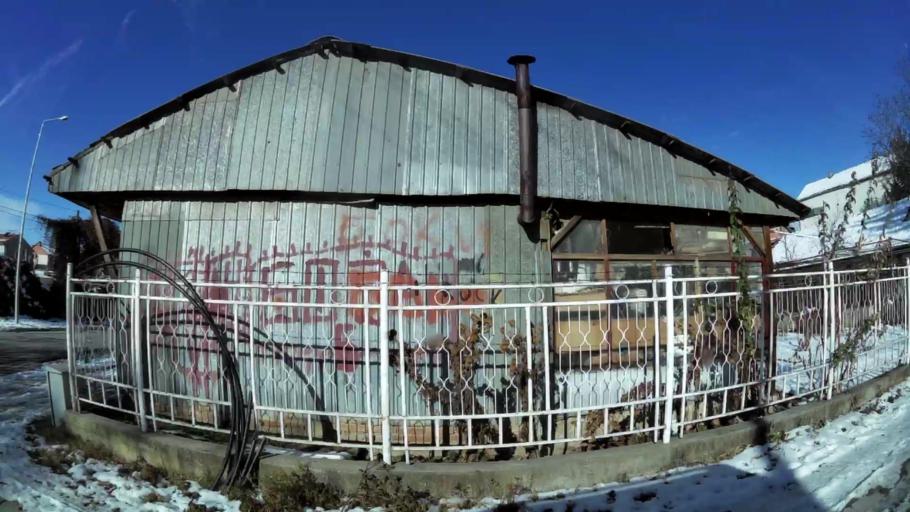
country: MK
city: Krushopek
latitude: 42.0052
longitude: 21.3618
